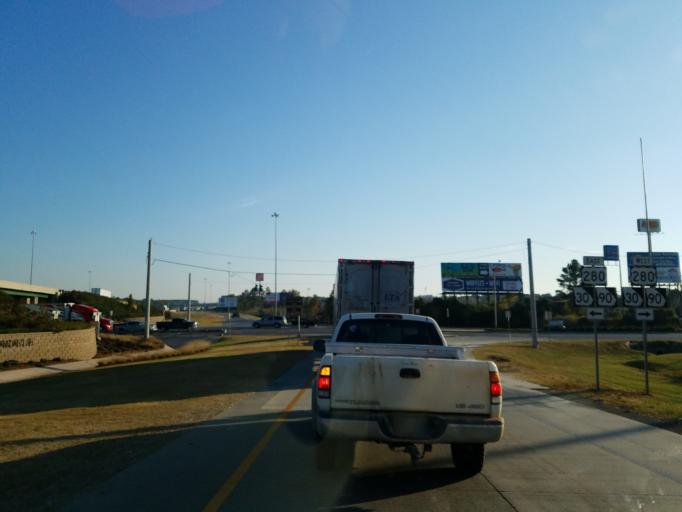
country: US
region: Georgia
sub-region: Crisp County
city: Cordele
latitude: 31.9608
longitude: -83.7522
